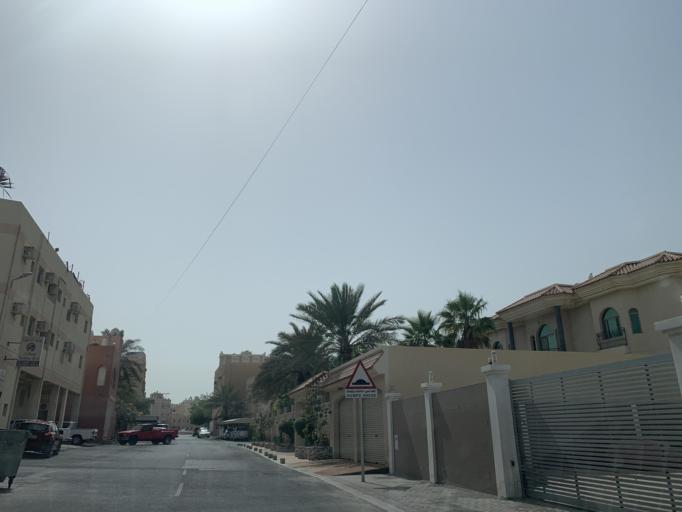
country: BH
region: Northern
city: Ar Rifa'
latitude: 26.1222
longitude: 50.5768
